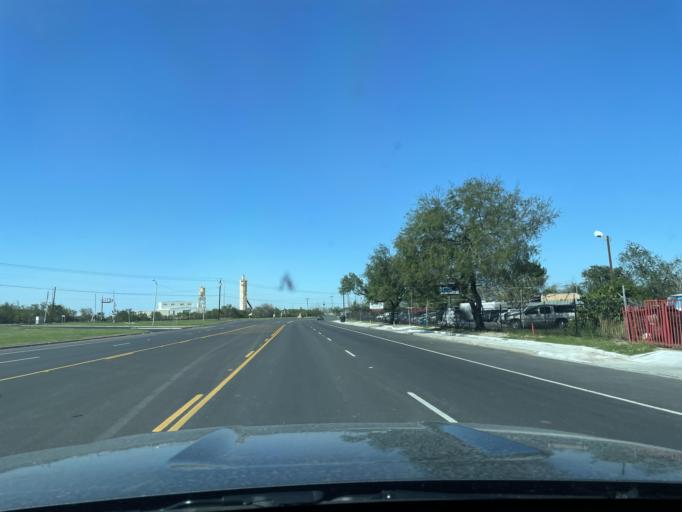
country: US
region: Texas
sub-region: Cameron County
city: Harlingen
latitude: 26.2156
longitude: -97.7113
